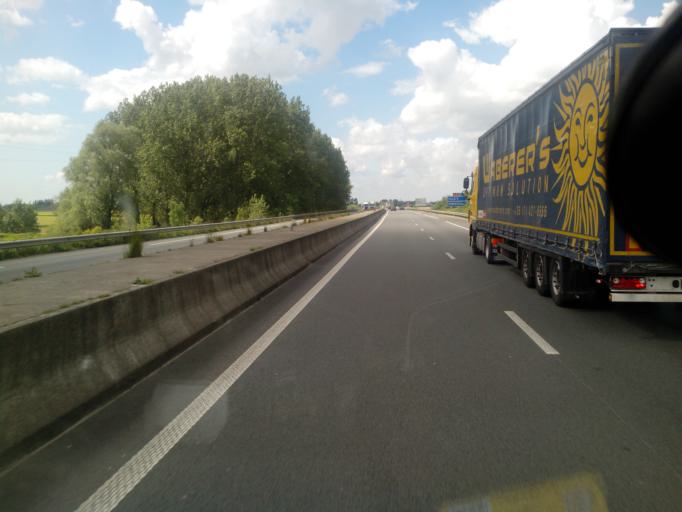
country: FR
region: Nord-Pas-de-Calais
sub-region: Departement du Nord
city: Herzeele
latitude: 50.8901
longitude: 2.5104
